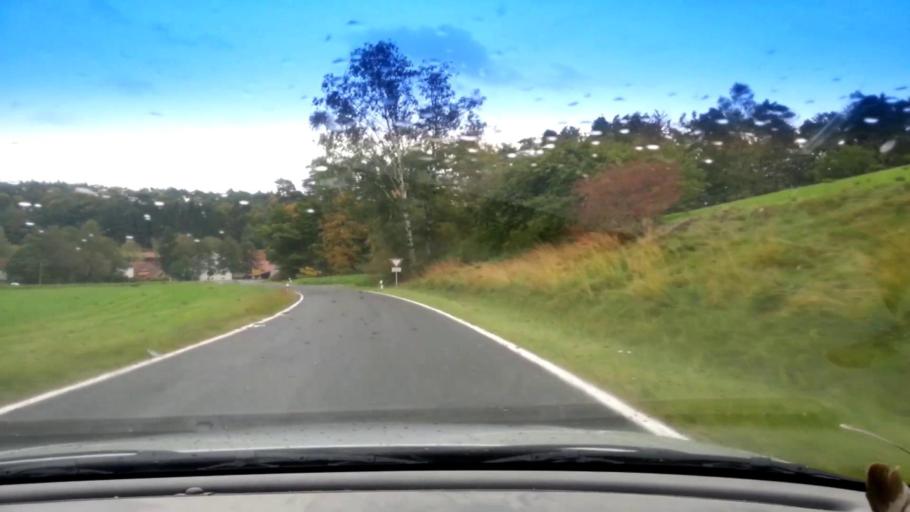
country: DE
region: Bavaria
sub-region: Regierungsbezirk Unterfranken
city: Kirchlauter
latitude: 50.0264
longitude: 10.7338
